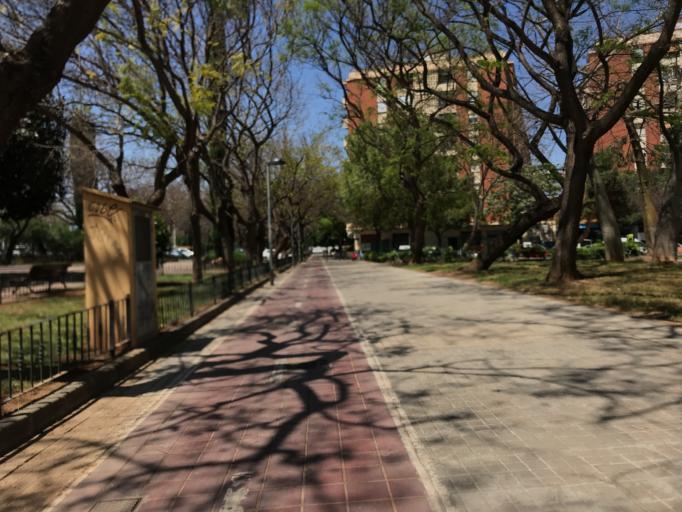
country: ES
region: Valencia
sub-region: Provincia de Valencia
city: Mislata
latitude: 39.4607
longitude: -0.4036
